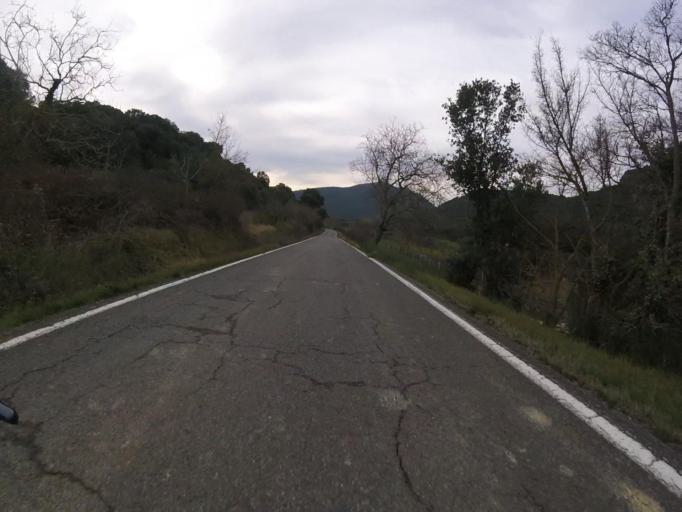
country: ES
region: Navarre
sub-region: Provincia de Navarra
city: Estella
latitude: 42.7069
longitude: -2.0511
